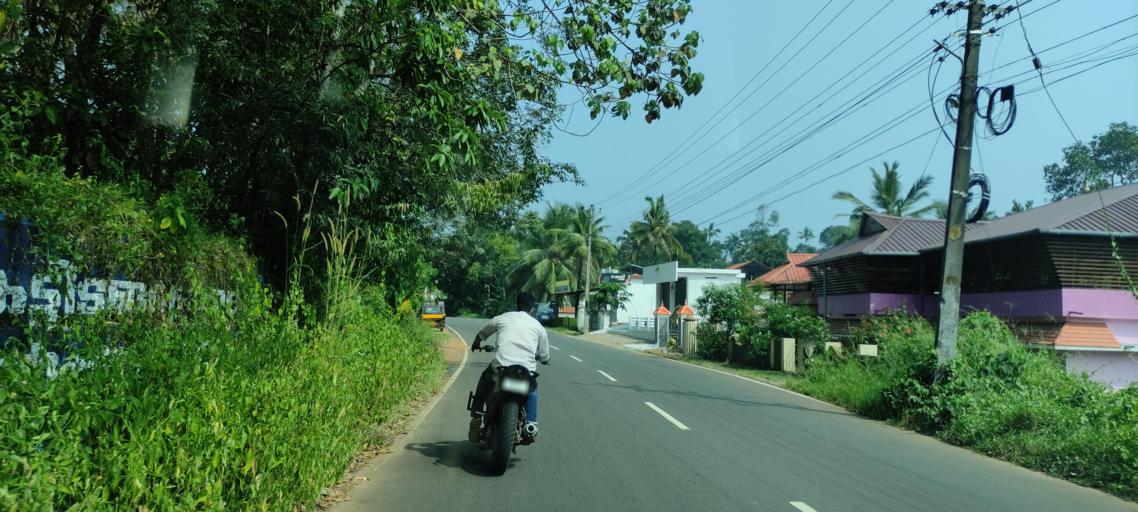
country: IN
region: Kerala
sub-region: Pattanamtitta
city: Adur
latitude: 9.2427
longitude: 76.6767
